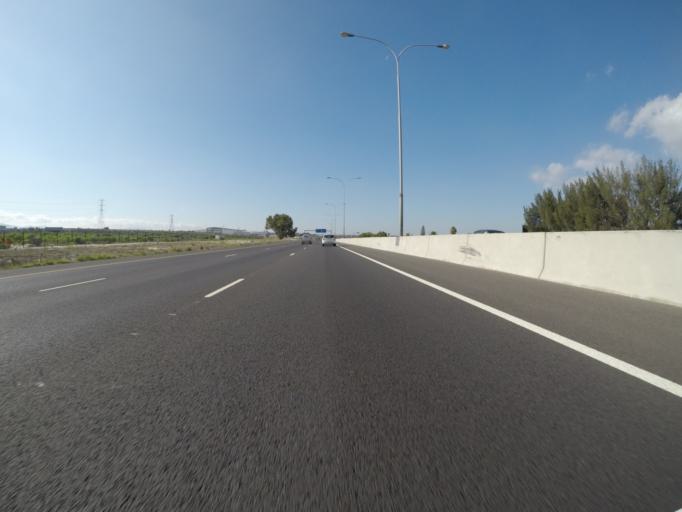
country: ZA
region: Western Cape
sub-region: City of Cape Town
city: Kraaifontein
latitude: -33.9256
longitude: 18.6632
